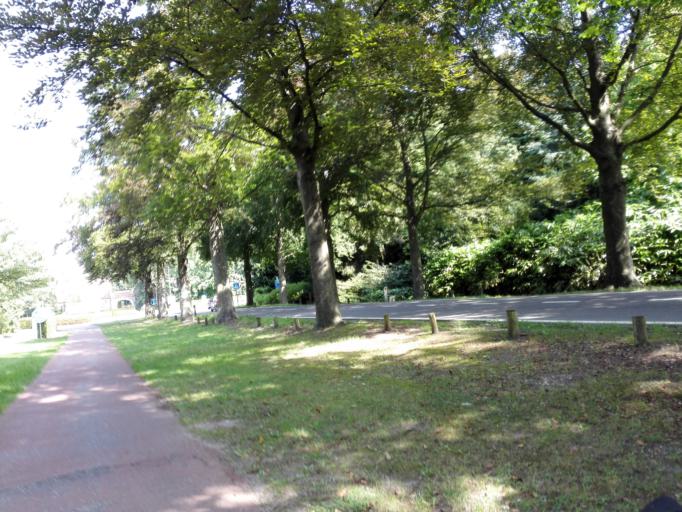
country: BE
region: Flanders
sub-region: Provincie Limburg
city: Zonhoven
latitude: 50.9583
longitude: 5.4076
